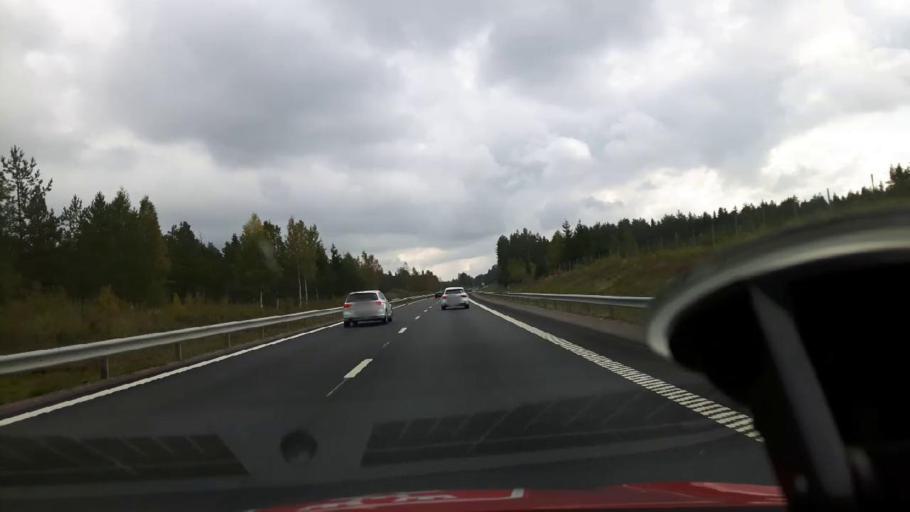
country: SE
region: Gaevleborg
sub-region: Gavle Kommun
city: Gavle
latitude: 60.6029
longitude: 17.1818
